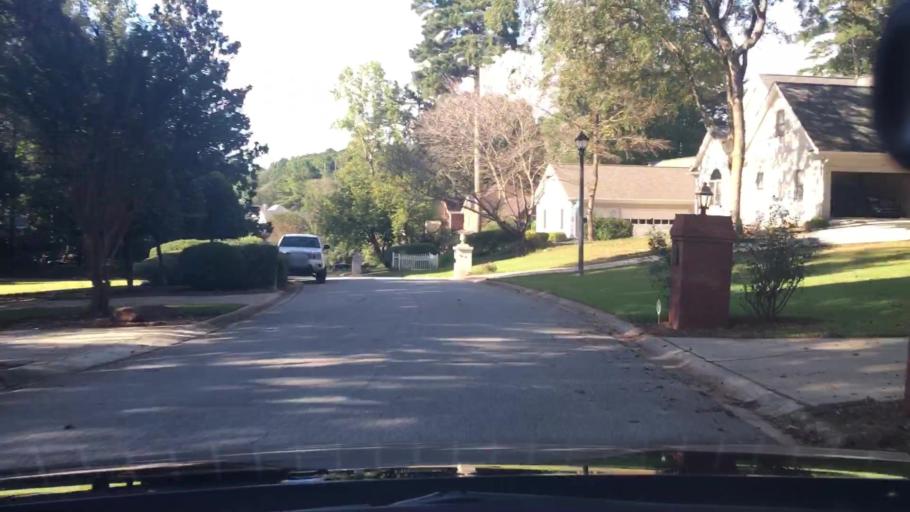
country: US
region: Georgia
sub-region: Coweta County
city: East Newnan
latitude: 33.3958
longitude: -84.7141
